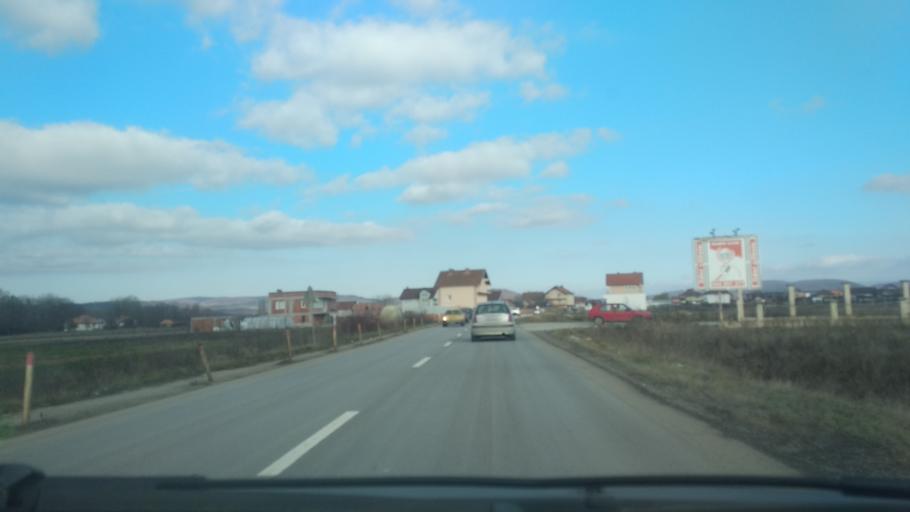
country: XK
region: Pristina
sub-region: Komuna e Obiliqit
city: Obiliq
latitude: 42.7306
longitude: 21.1031
